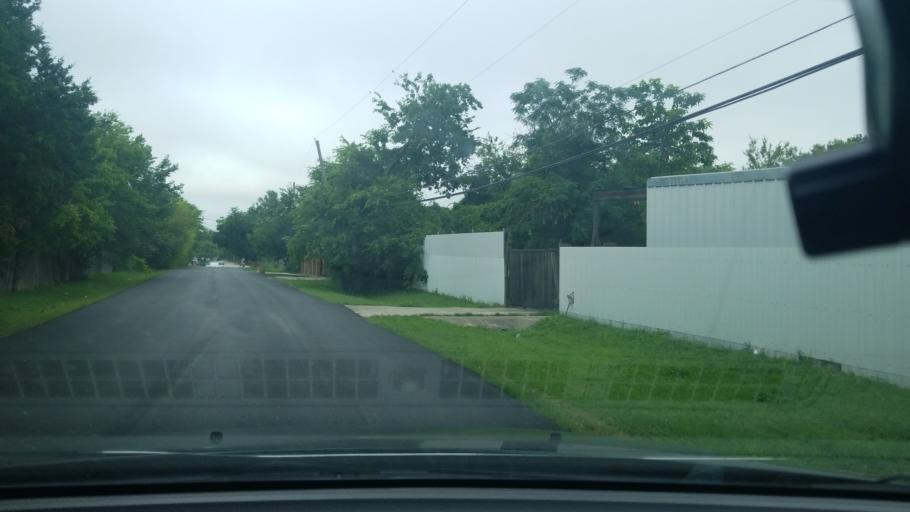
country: US
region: Texas
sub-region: Dallas County
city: Balch Springs
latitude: 32.7724
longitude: -96.6891
